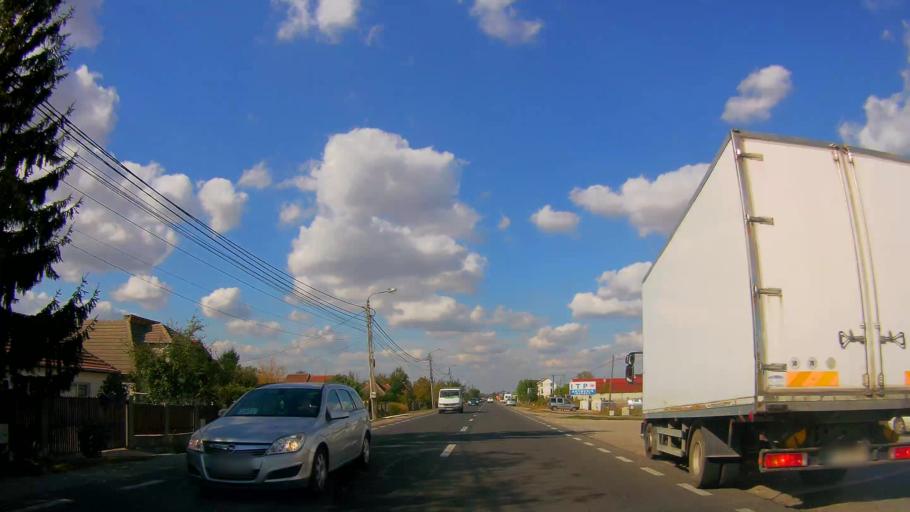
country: RO
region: Satu Mare
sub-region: Comuna Paulesti
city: Paulesti
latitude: 47.7527
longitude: 22.8831
